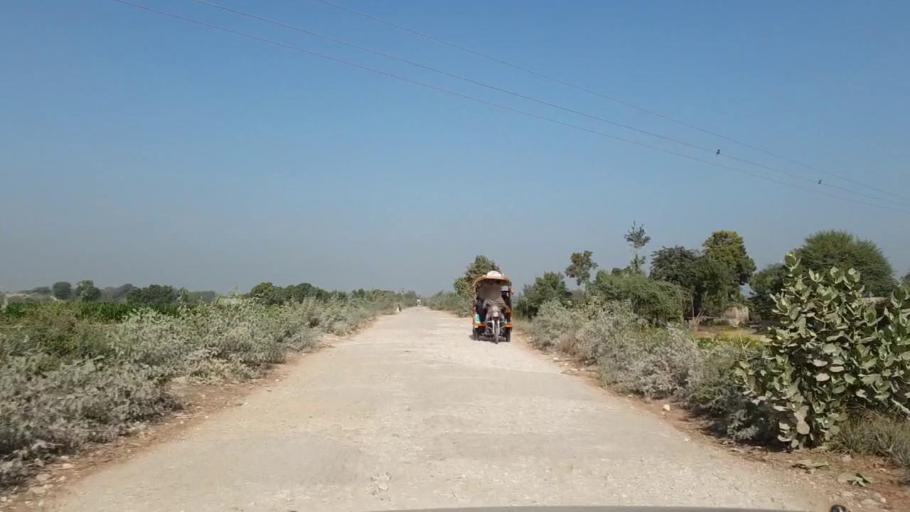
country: PK
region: Sindh
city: Matiari
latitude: 25.5785
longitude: 68.6044
